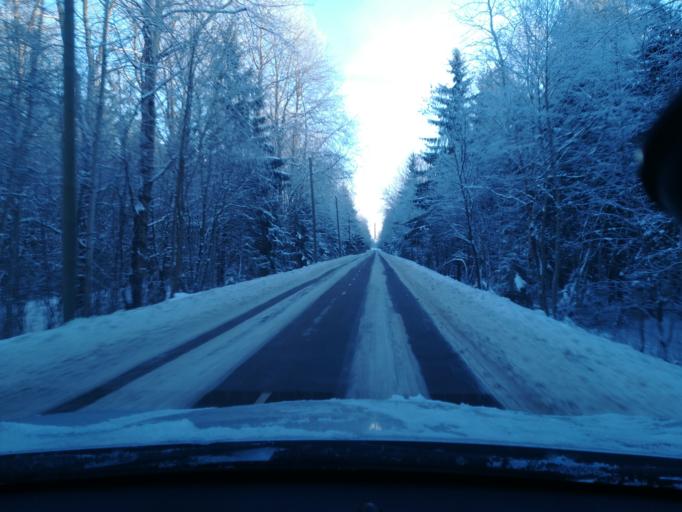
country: EE
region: Harju
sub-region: Saue vald
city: Laagri
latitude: 59.3892
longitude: 24.6183
